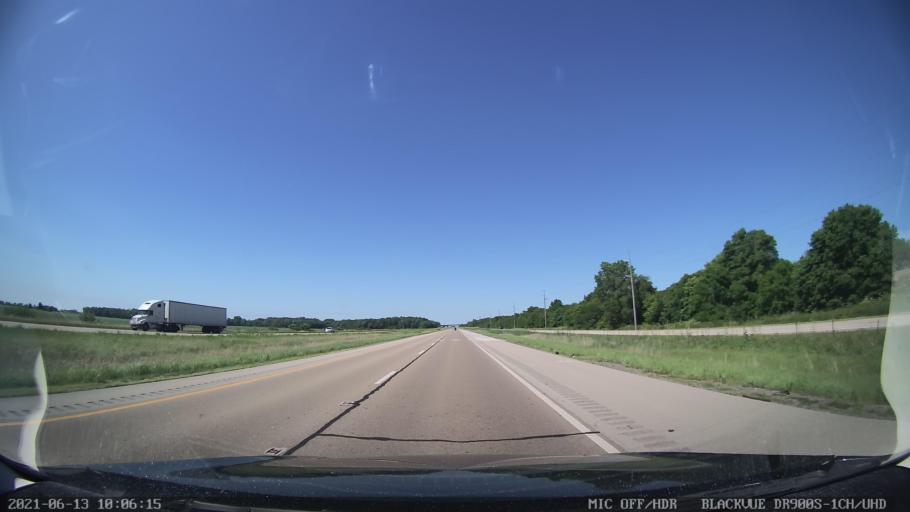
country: US
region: Illinois
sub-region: Logan County
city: Atlanta
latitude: 40.2308
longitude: -89.2668
